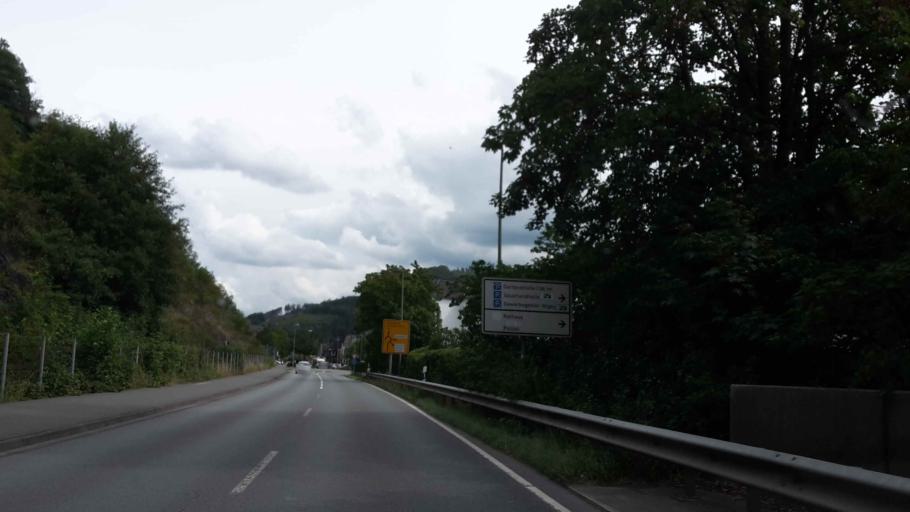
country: DE
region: North Rhine-Westphalia
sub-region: Regierungsbezirk Arnsberg
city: Lennestadt
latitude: 51.1061
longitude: 8.0780
